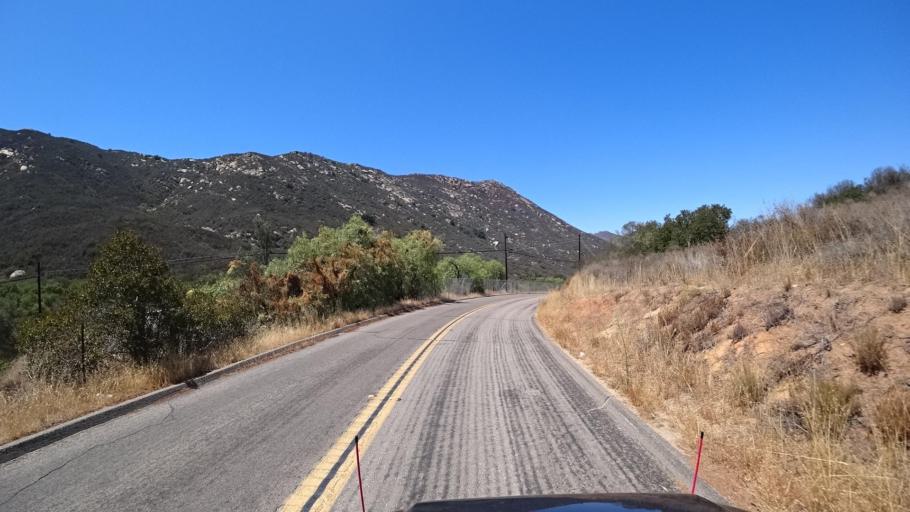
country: US
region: California
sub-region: San Diego County
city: Rainbow
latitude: 33.3431
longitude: -117.0829
